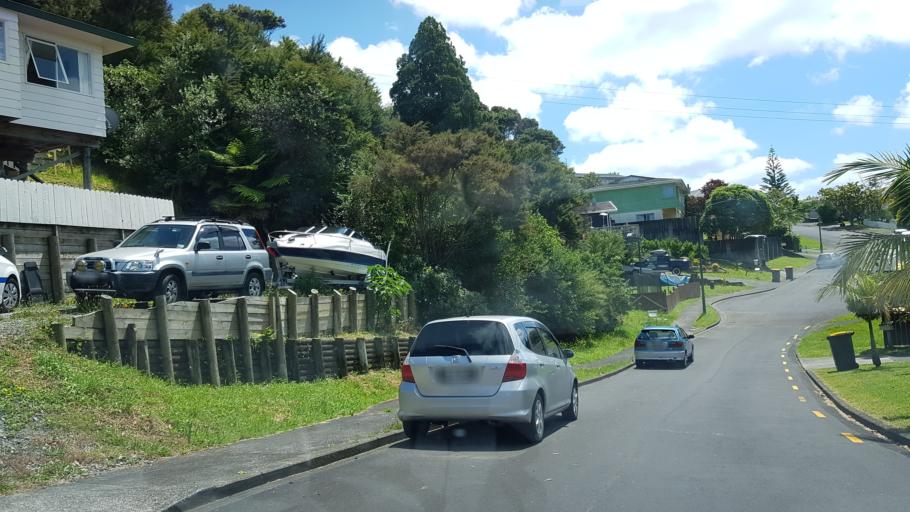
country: NZ
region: Auckland
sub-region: Auckland
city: North Shore
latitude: -36.7784
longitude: 174.7116
